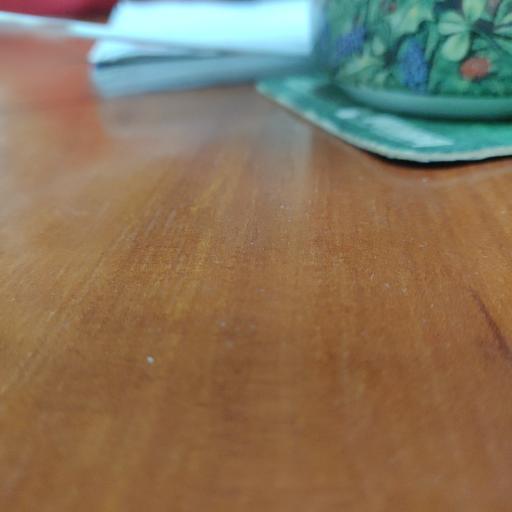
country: LV
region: Ozolnieku
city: Ozolnieki
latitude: 56.6542
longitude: 23.9134
